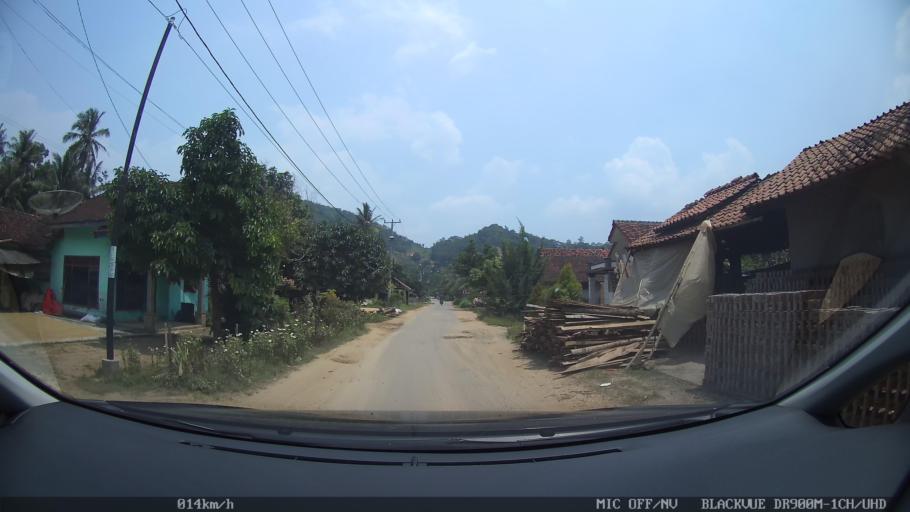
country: ID
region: Lampung
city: Pringsewu
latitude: -5.3791
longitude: 105.0000
